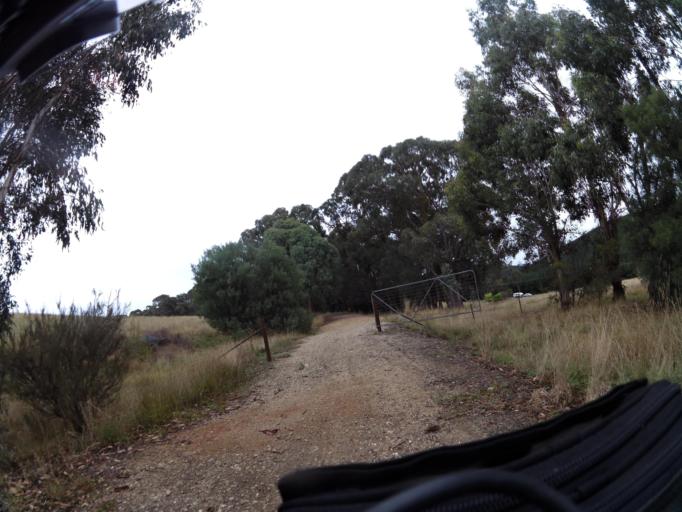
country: AU
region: New South Wales
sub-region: Greater Hume Shire
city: Holbrook
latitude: -36.1525
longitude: 147.4867
